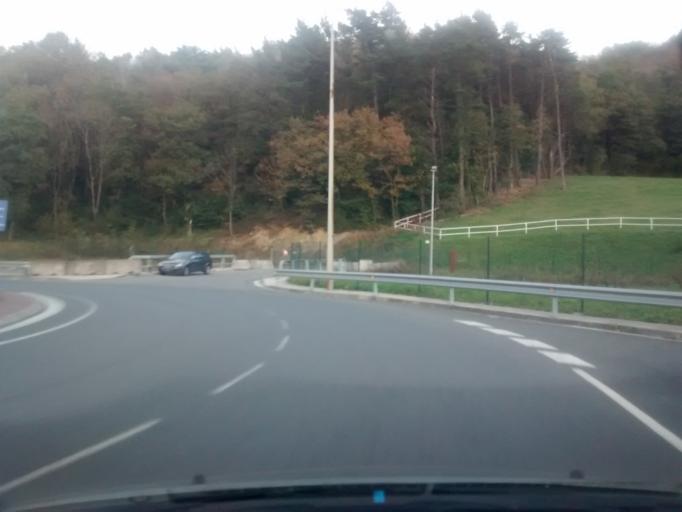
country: ES
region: Basque Country
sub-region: Provincia de Guipuzcoa
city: Lasarte
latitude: 43.2828
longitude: -2.0016
